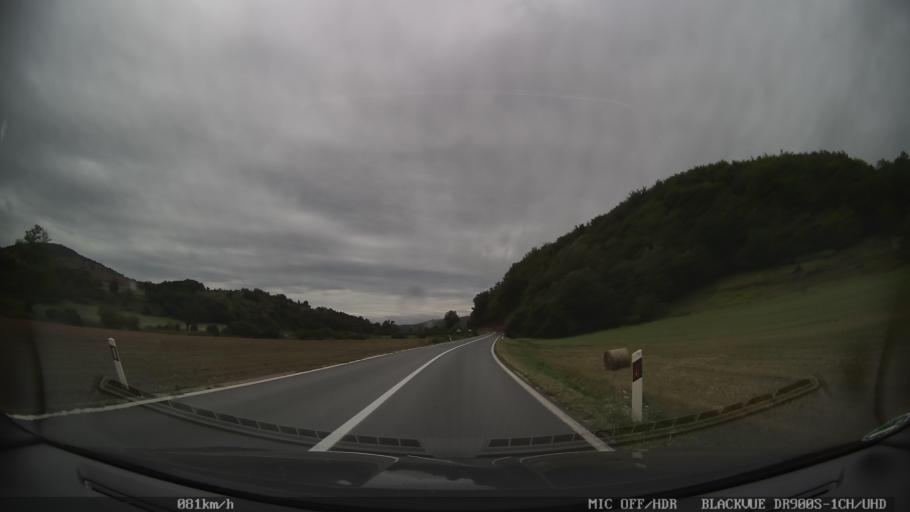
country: HR
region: Licko-Senjska
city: Brinje
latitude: 44.9314
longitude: 15.1332
